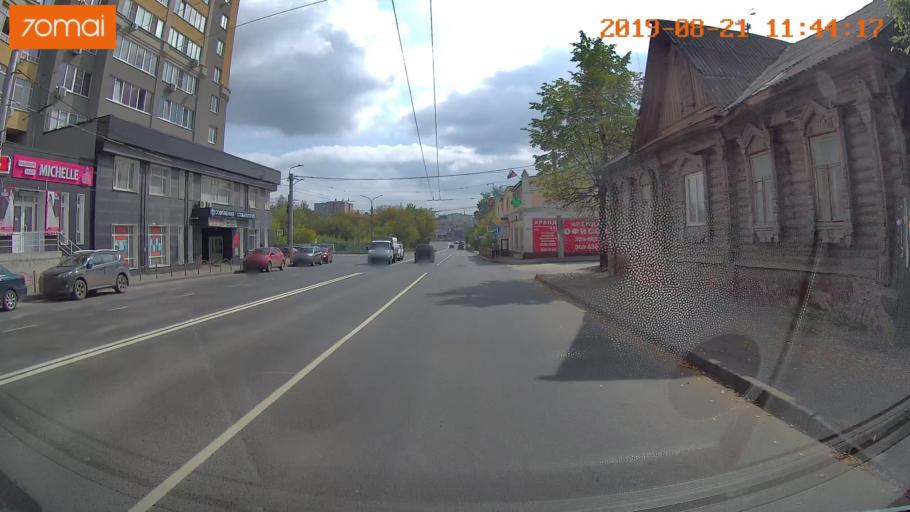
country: RU
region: Ivanovo
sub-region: Gorod Ivanovo
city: Ivanovo
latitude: 56.9986
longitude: 40.9671
